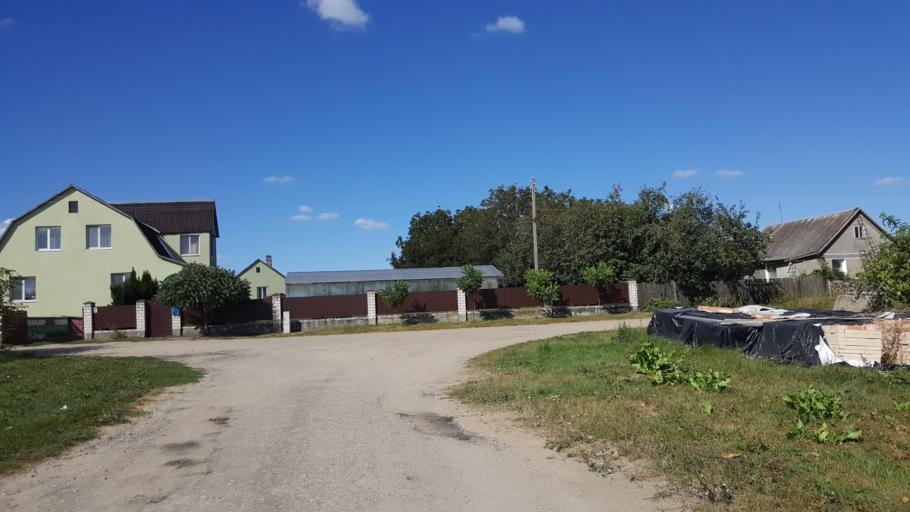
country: BY
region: Brest
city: Vysokaye
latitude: 52.2740
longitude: 23.4919
